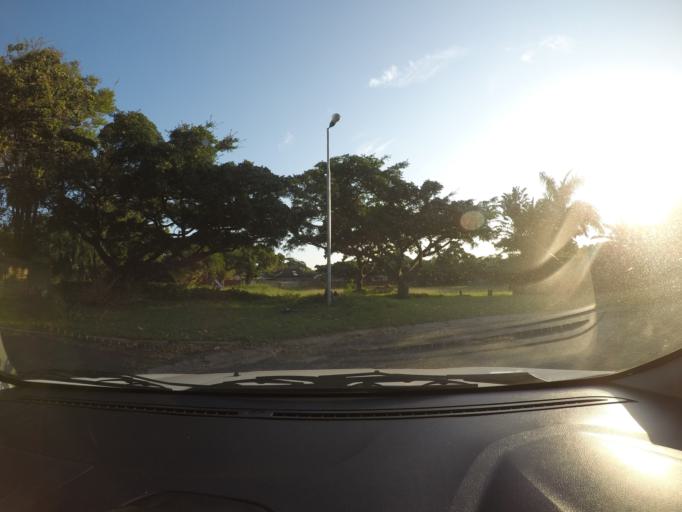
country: ZA
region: KwaZulu-Natal
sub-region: uThungulu District Municipality
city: Richards Bay
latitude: -28.7815
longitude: 32.0984
